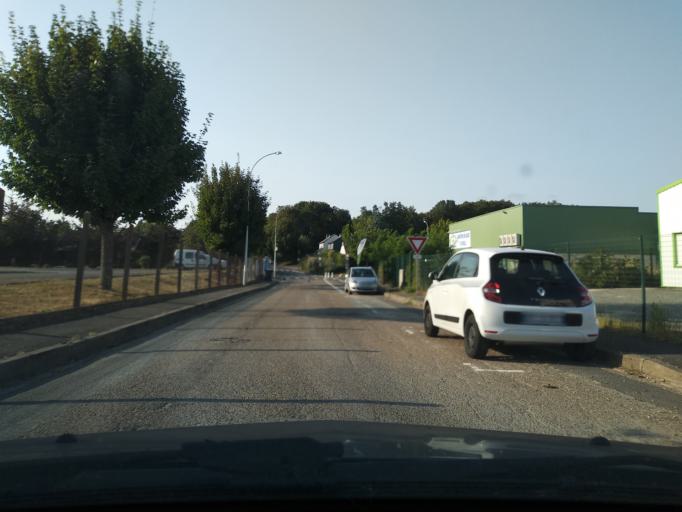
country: FR
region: Centre
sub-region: Departement d'Indre-et-Loire
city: Saint-Cyr-sur-Loire
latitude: 47.4312
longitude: 0.6831
